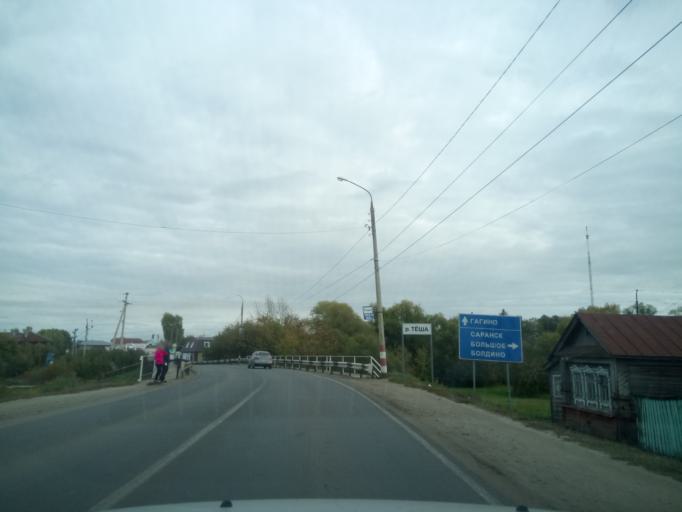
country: RU
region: Nizjnij Novgorod
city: Lukoyanov
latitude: 55.0298
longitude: 44.4895
